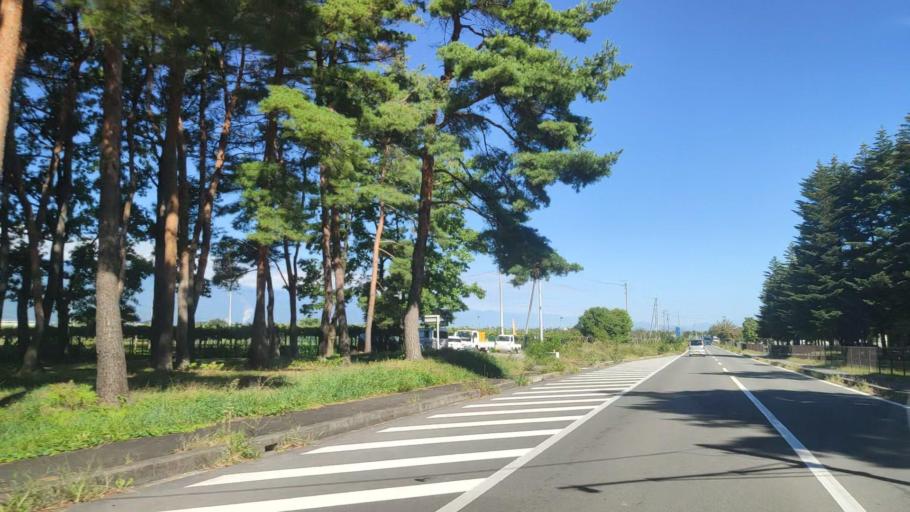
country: JP
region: Nagano
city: Shiojiri
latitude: 36.1627
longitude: 137.9175
